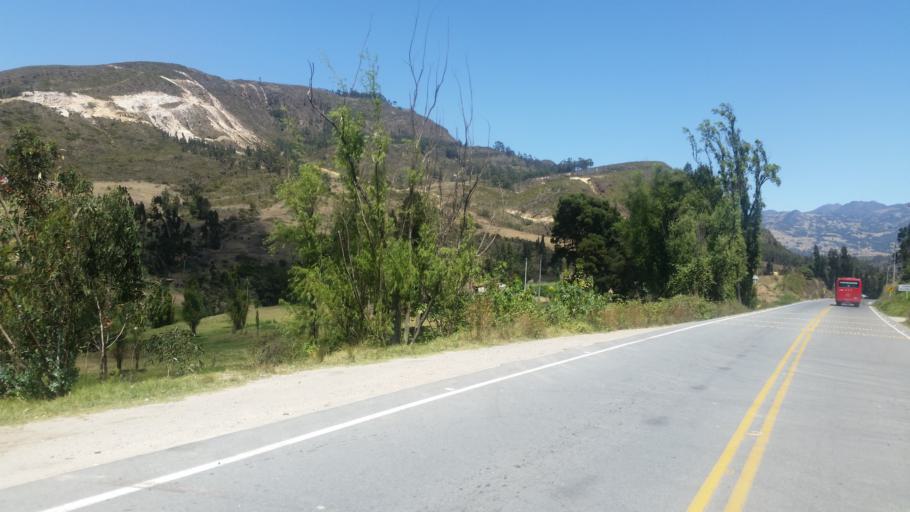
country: CO
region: Boyaca
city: Topaga
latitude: 5.7731
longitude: -72.8596
